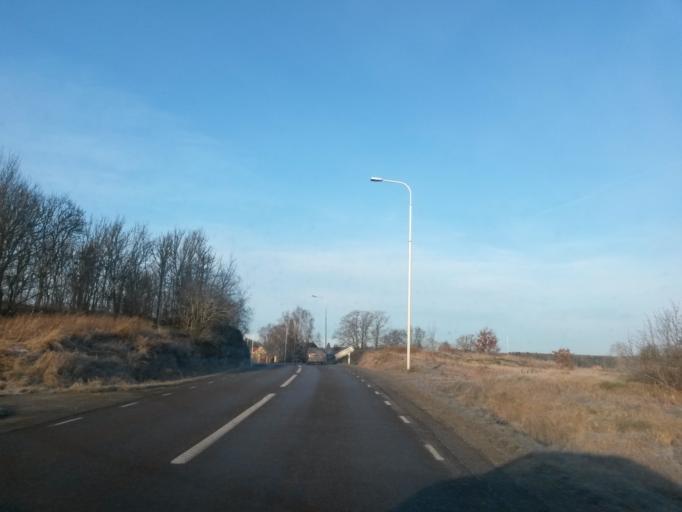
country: SE
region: Vaestra Goetaland
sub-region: Vanersborgs Kommun
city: Vargon
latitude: 58.2468
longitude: 12.4236
